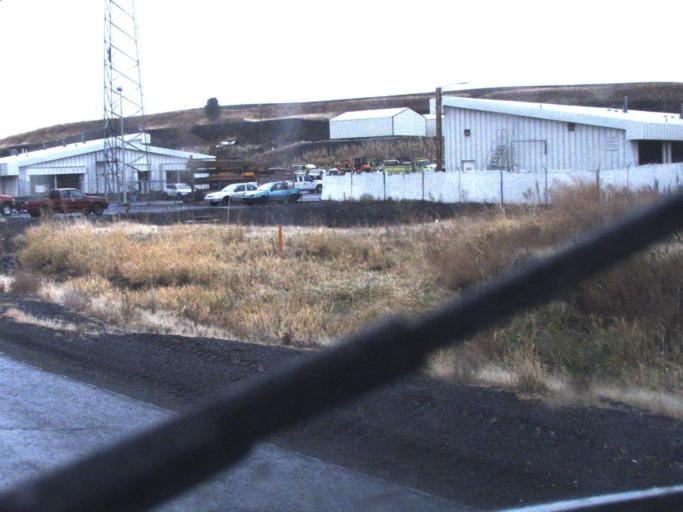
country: US
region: Washington
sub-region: Whitman County
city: Colfax
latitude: 46.9573
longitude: -117.3326
